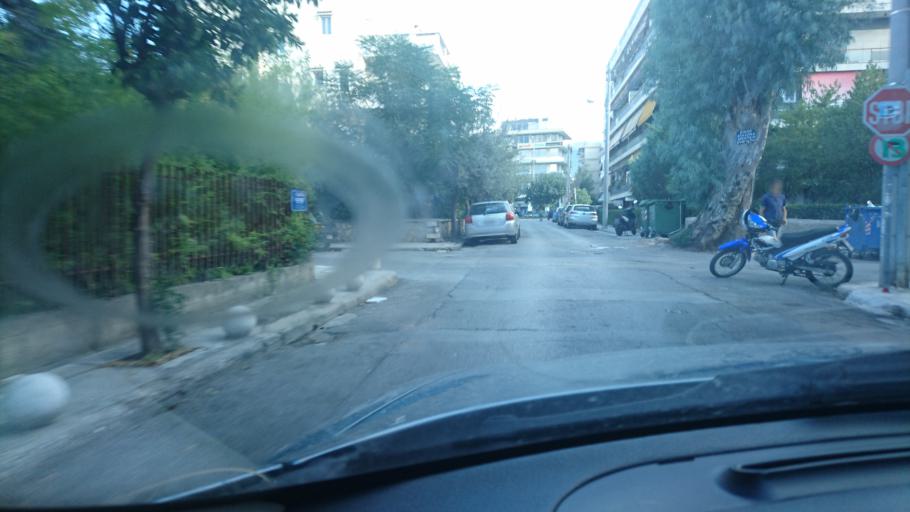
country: GR
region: Attica
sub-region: Nomarchia Athinas
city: Cholargos
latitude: 38.0077
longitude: 23.7994
